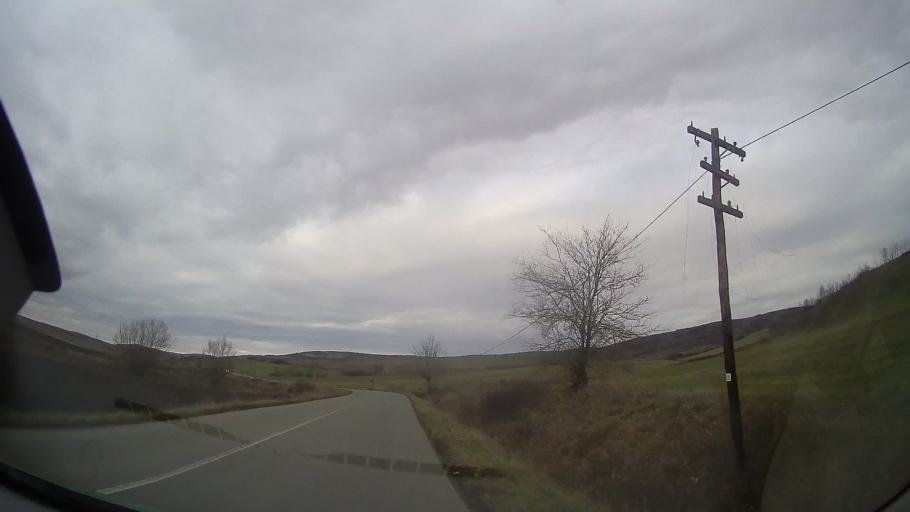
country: RO
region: Mures
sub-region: Comuna Faragau
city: Faragau
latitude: 46.7412
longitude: 24.5375
